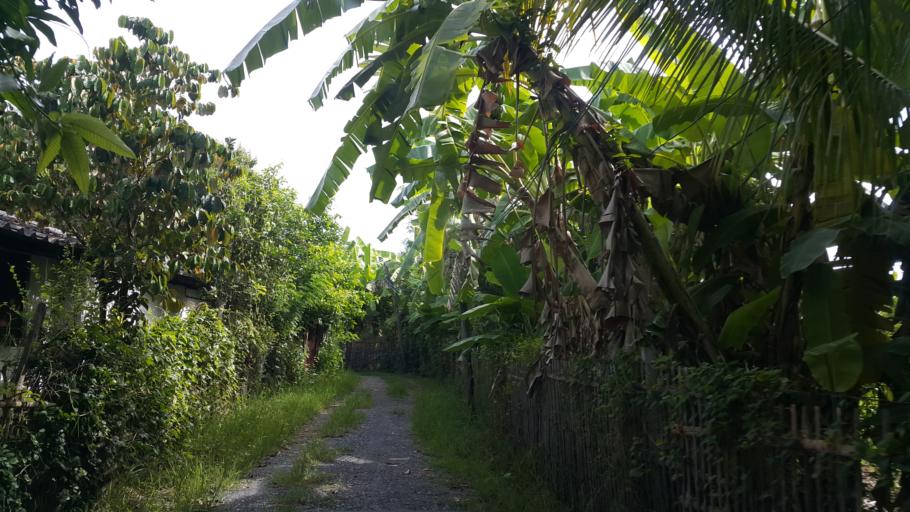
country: TH
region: Chiang Mai
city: San Kamphaeng
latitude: 18.7216
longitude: 99.0897
